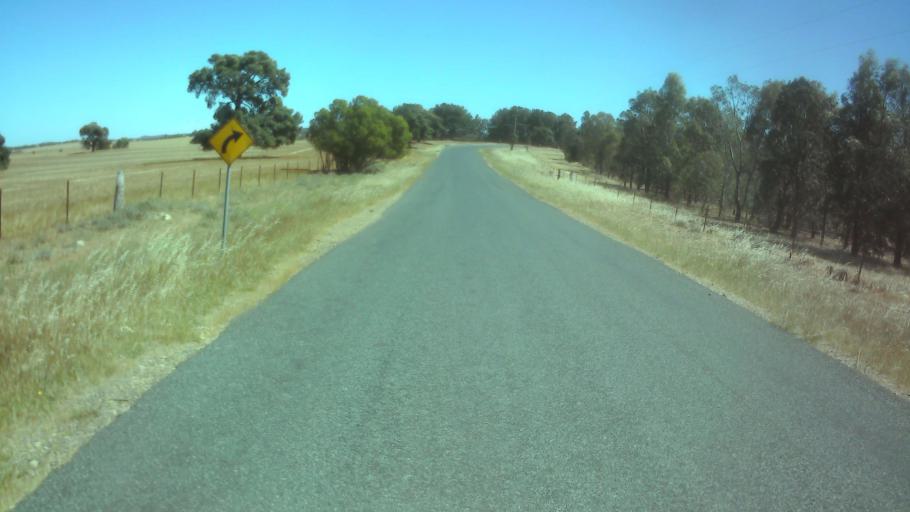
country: AU
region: New South Wales
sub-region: Weddin
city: Grenfell
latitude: -33.9569
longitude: 148.4001
